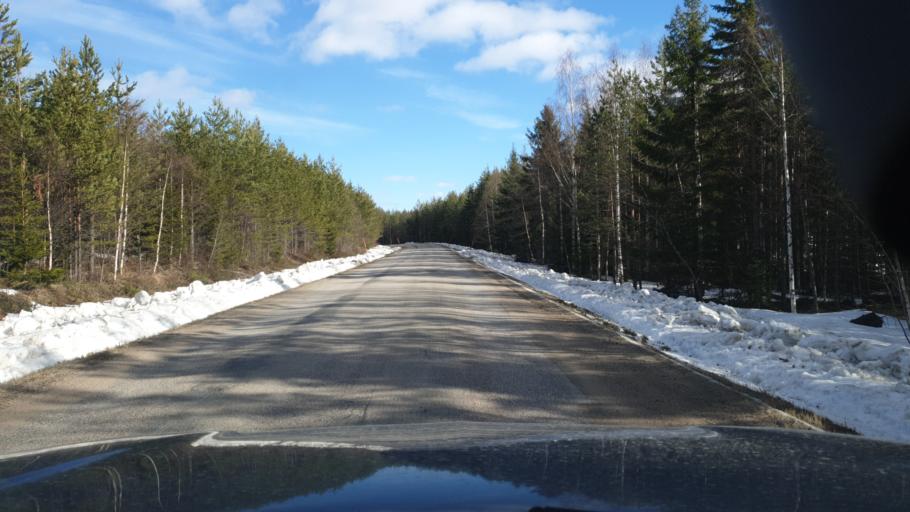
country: SE
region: Gaevleborg
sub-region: Ljusdals Kommun
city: Farila
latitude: 61.8450
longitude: 15.9474
